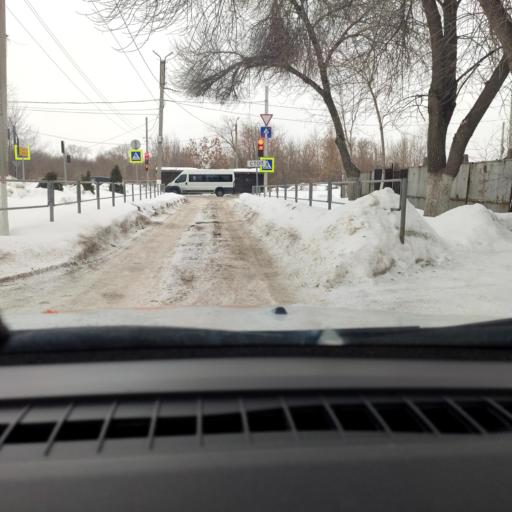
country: RU
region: Samara
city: Novokuybyshevsk
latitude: 53.1149
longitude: 49.9332
